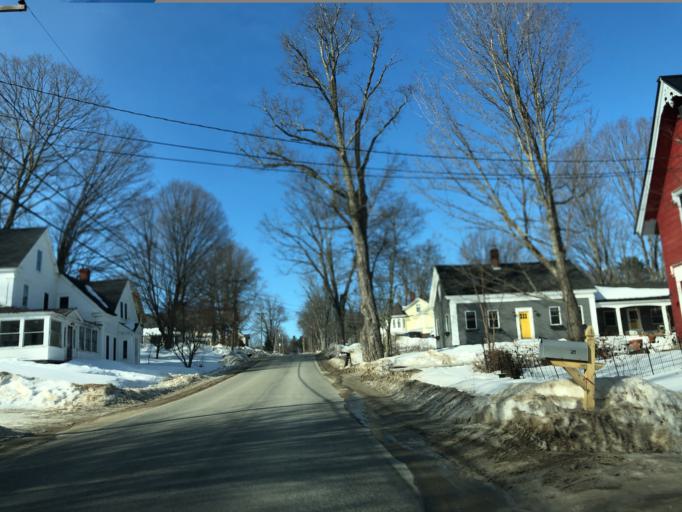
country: US
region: Maine
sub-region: Oxford County
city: Buckfield
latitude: 44.2916
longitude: -70.3669
